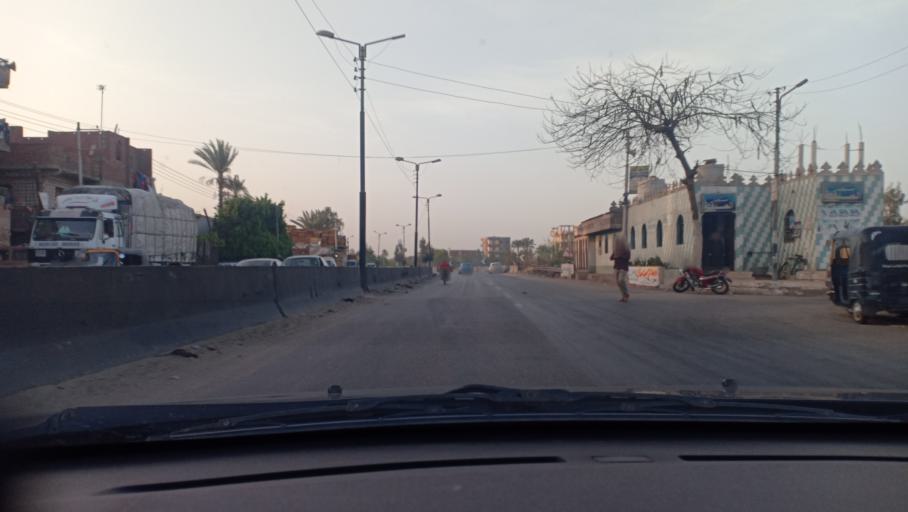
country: EG
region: Muhafazat al Gharbiyah
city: Zifta
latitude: 30.6709
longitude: 31.2859
